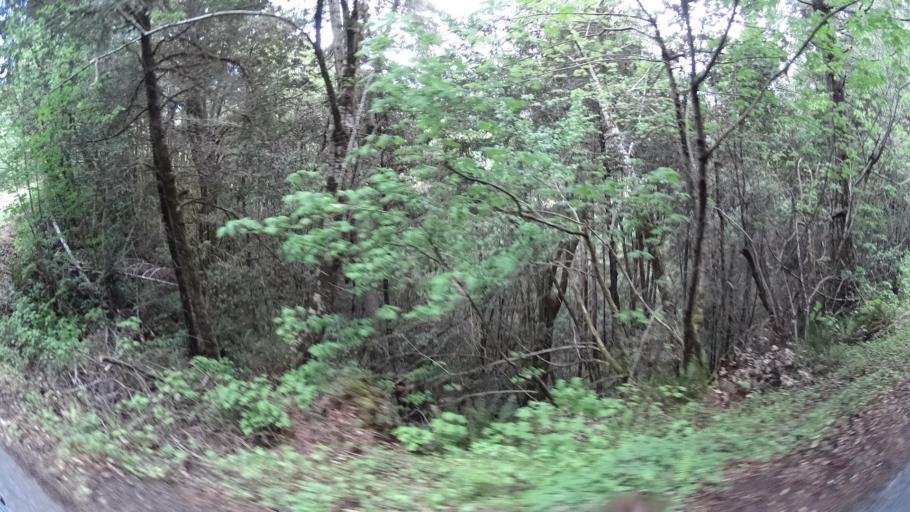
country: US
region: California
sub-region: Humboldt County
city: Blue Lake
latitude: 40.7591
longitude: -123.9083
